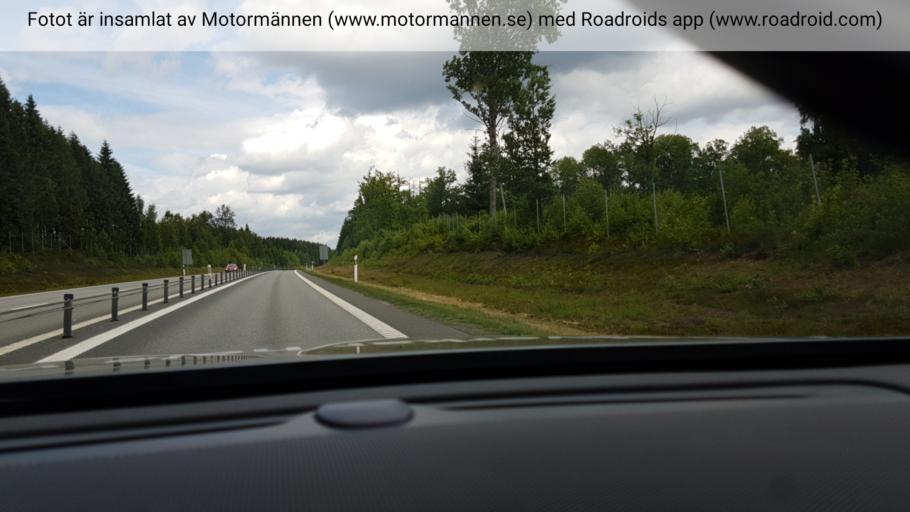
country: SE
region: Skane
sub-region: Hassleholms Kommun
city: Hassleholm
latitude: 56.1878
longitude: 13.8461
